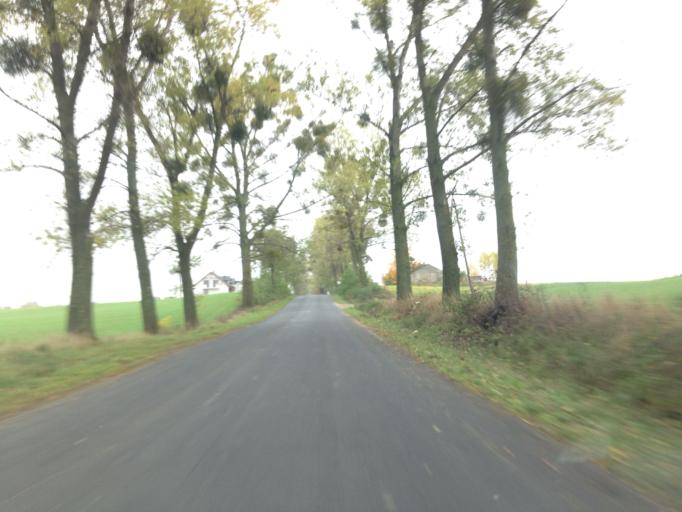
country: PL
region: Kujawsko-Pomorskie
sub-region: Powiat brodnicki
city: Gorzno
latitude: 53.2139
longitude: 19.6200
